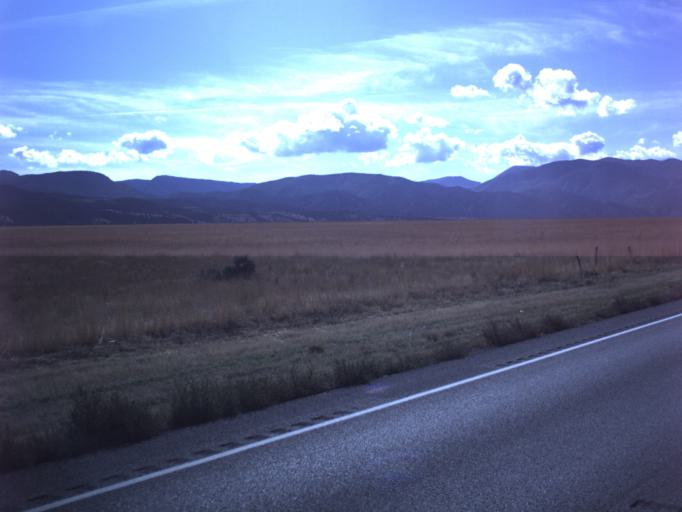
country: US
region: Utah
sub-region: Juab County
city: Nephi
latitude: 39.6245
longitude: -111.8618
